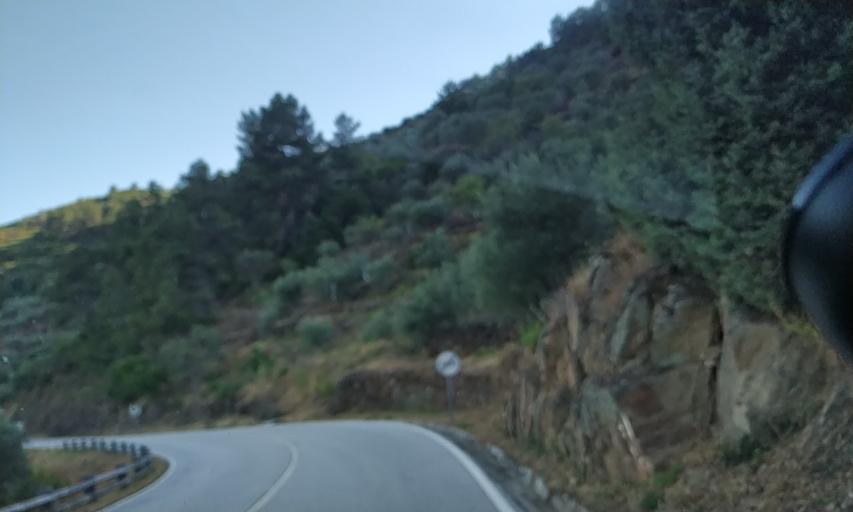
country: PT
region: Viseu
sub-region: Sao Joao da Pesqueira
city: Sao Joao da Pesqueira
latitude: 41.2344
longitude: -7.4295
